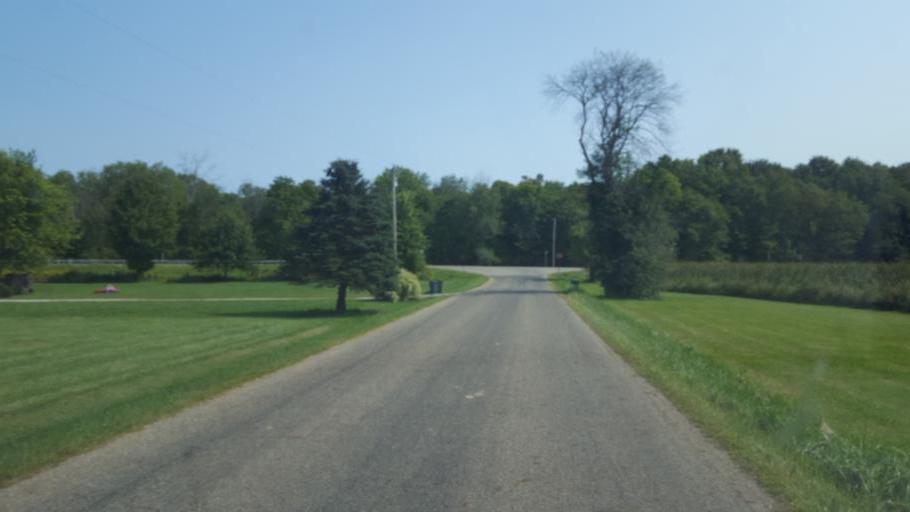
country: US
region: Ohio
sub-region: Knox County
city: Danville
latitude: 40.4889
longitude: -82.3551
